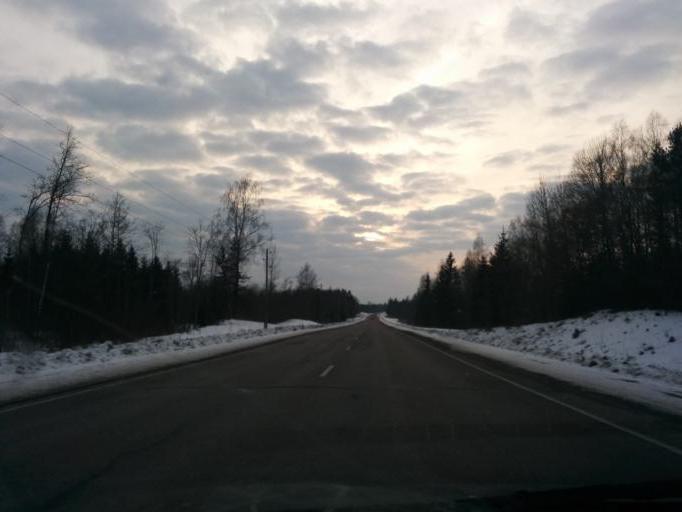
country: LV
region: Smiltene
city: Smiltene
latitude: 57.3237
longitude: 25.7827
